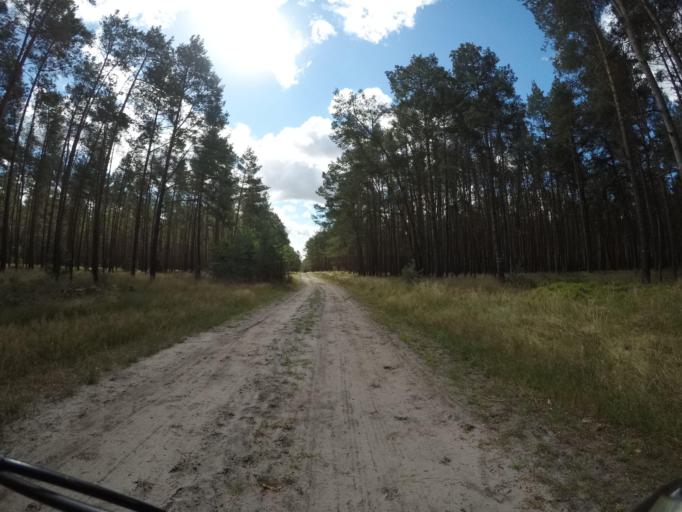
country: DE
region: Lower Saxony
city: Hitzacker
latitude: 53.2240
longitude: 11.0350
